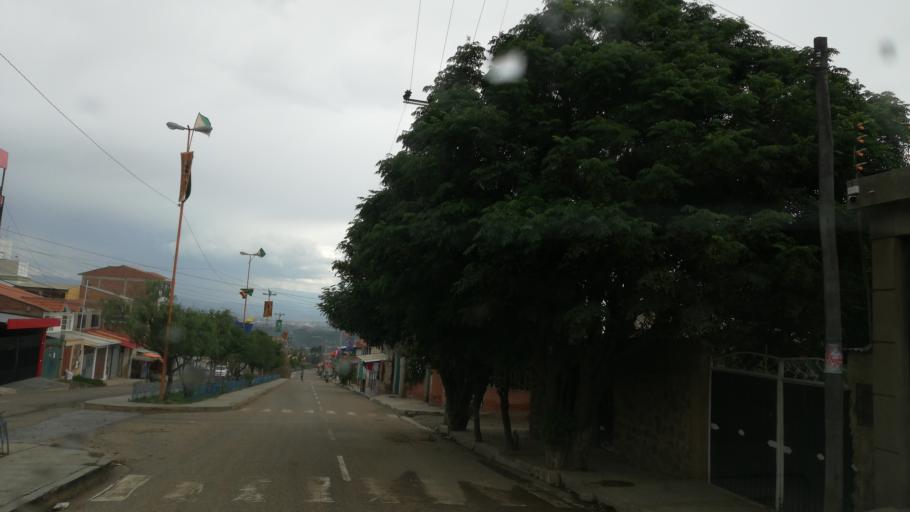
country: BO
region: Cochabamba
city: Cochabamba
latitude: -17.3338
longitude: -66.1972
